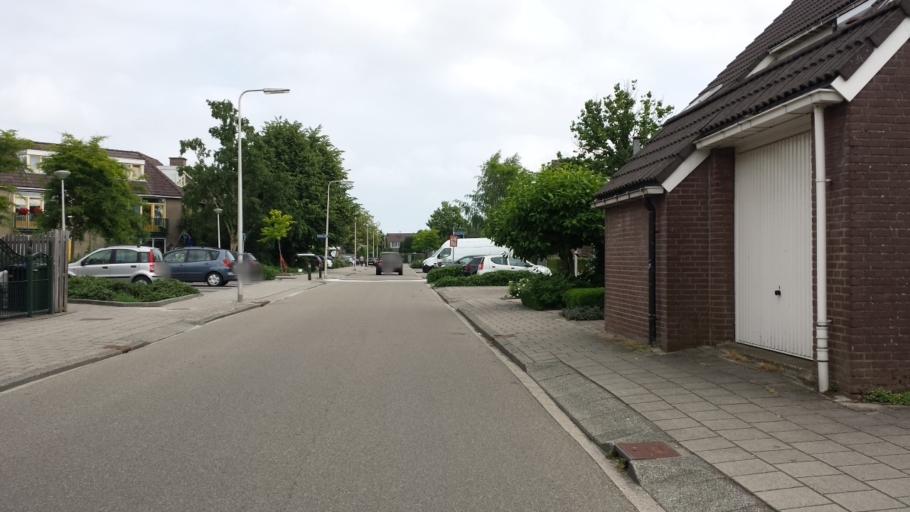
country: NL
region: South Holland
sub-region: Bodegraven-Reeuwijk
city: Reeuwijk
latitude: 52.0486
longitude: 4.7286
